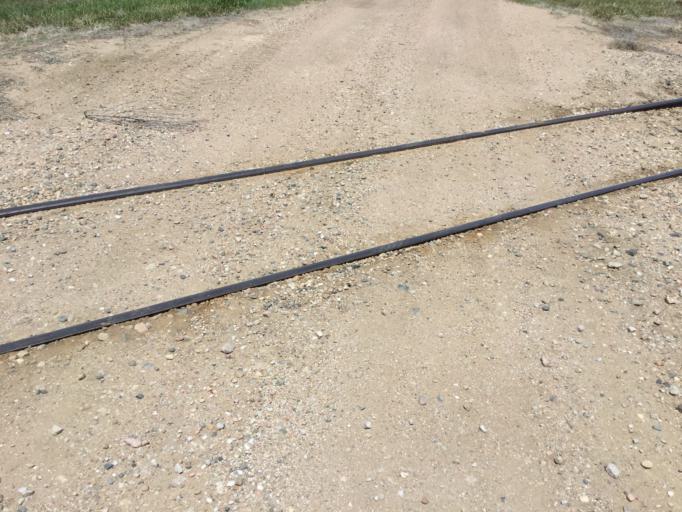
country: US
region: Kansas
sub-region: Sheridan County
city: Hoxie
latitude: 39.5910
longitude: -100.4606
